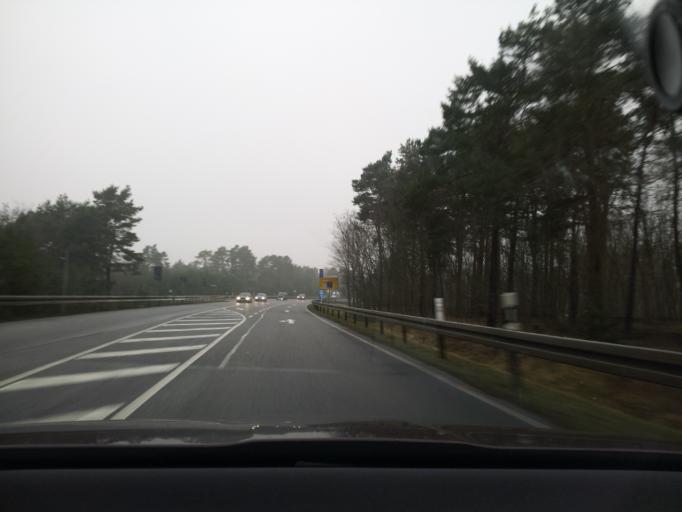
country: DE
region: Brandenburg
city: Langewahl
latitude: 52.3425
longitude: 14.1022
